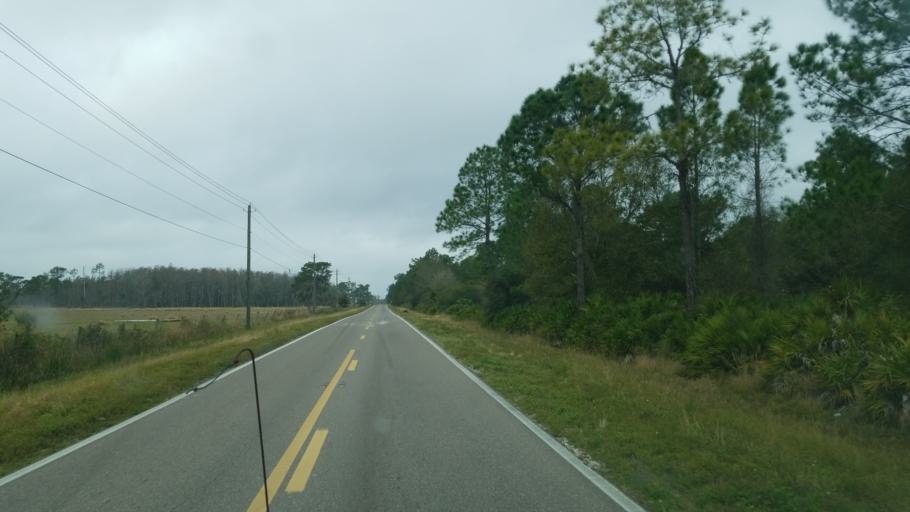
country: US
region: Florida
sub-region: Polk County
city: Polk City
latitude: 28.2586
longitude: -81.8387
